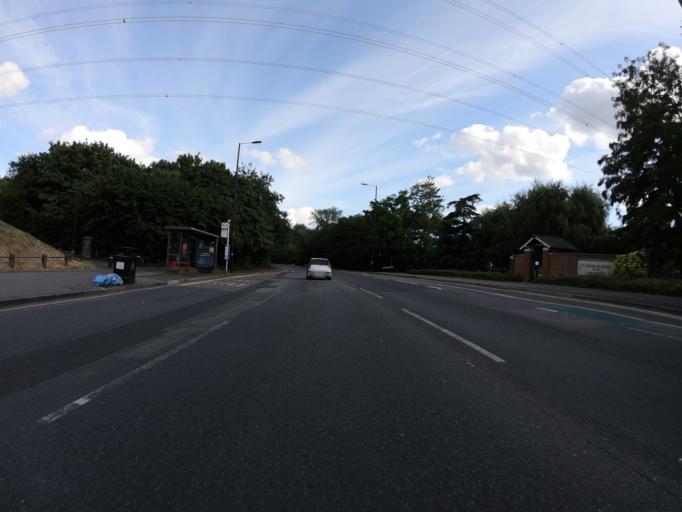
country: GB
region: England
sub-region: Greater London
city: East Ham
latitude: 51.5139
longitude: 0.0608
